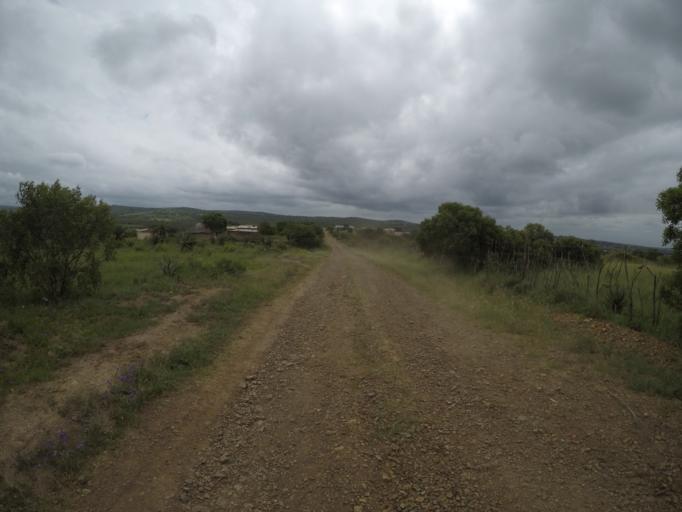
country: ZA
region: KwaZulu-Natal
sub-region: uThungulu District Municipality
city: Empangeni
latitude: -28.6013
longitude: 31.8337
